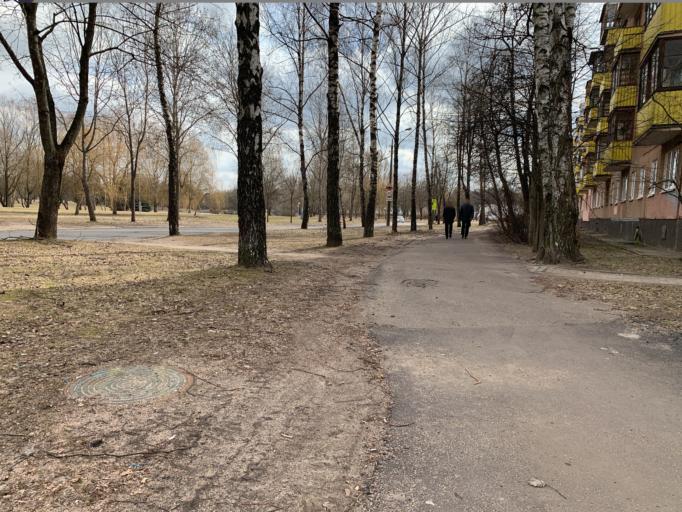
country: BY
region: Minsk
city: Borovlyany
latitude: 53.9513
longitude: 27.6289
